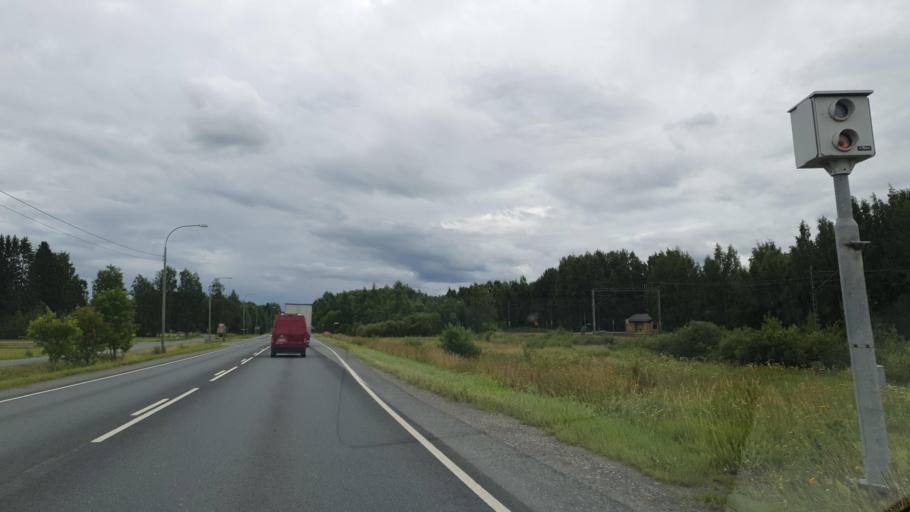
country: FI
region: Northern Savo
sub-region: Ylae-Savo
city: Lapinlahti
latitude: 63.4611
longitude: 27.3120
